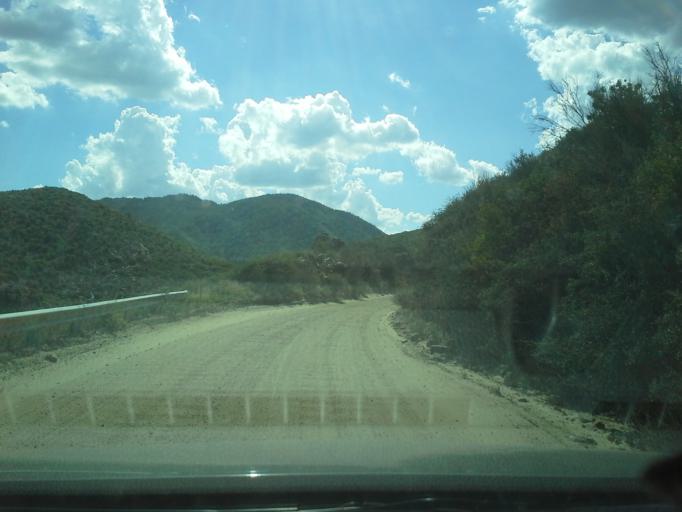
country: US
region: Arizona
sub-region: Yavapai County
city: Mayer
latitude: 34.2144
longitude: -112.3103
